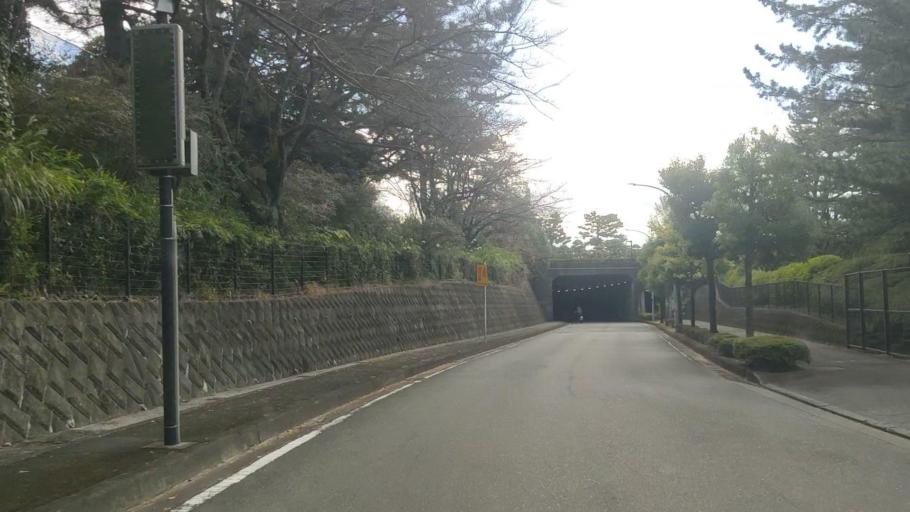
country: JP
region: Kanagawa
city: Yokohama
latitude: 35.4466
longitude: 139.5495
